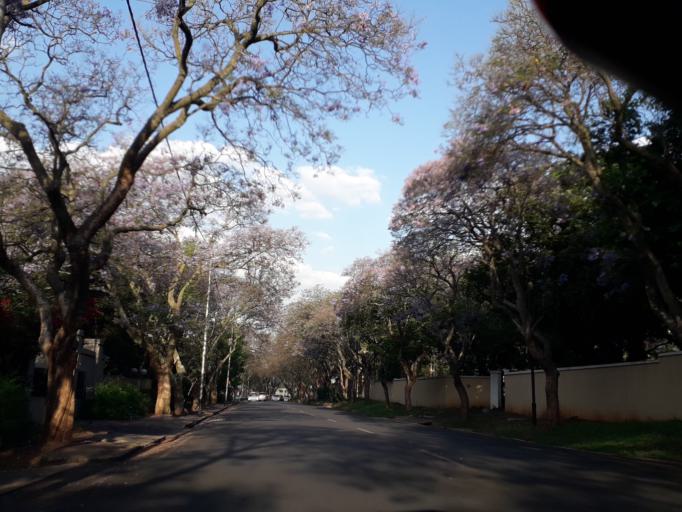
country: ZA
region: Gauteng
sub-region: City of Johannesburg Metropolitan Municipality
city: Johannesburg
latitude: -26.1706
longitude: 28.0600
